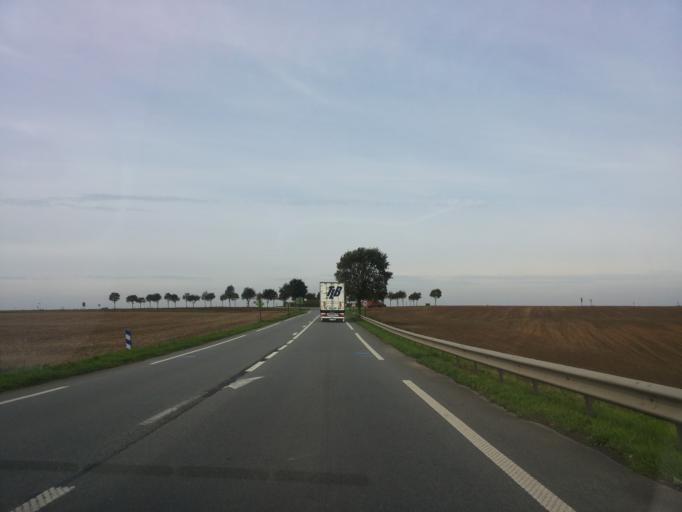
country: FR
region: Nord-Pas-de-Calais
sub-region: Departement du Nord
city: Lecluse
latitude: 50.2352
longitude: 2.9915
